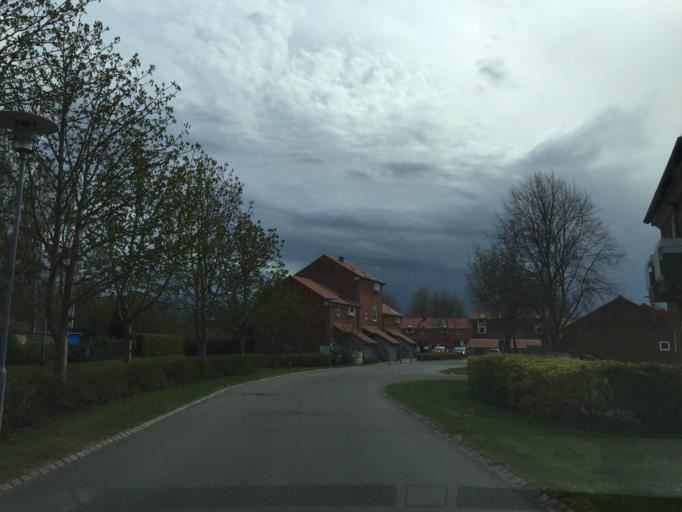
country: DK
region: South Denmark
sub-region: Odense Kommune
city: Neder Holluf
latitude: 55.3871
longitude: 10.4501
